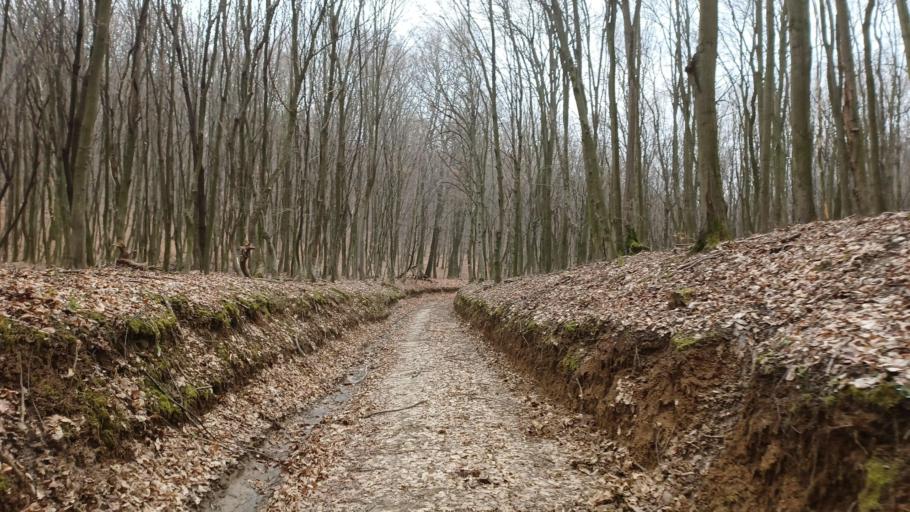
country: HU
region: Tolna
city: Szentgalpuszta
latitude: 46.3245
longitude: 18.6483
